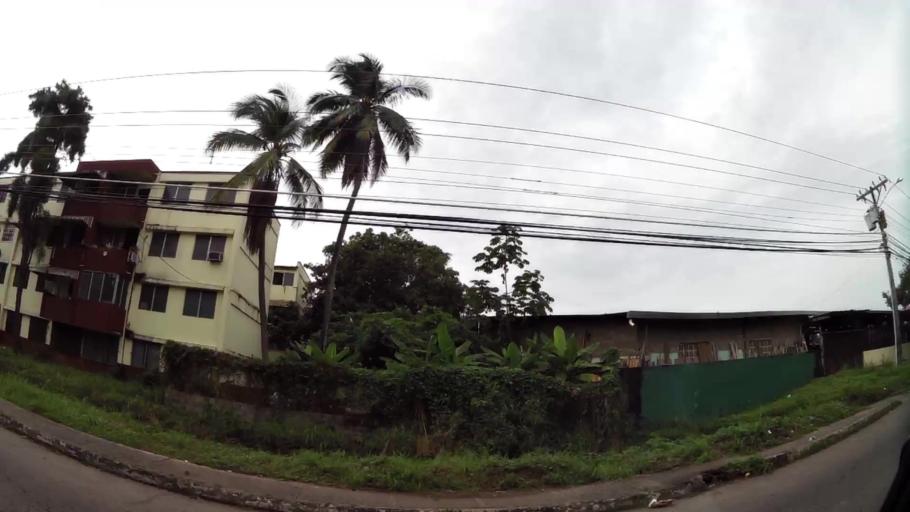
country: PA
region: Panama
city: San Miguelito
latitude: 9.0330
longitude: -79.4718
